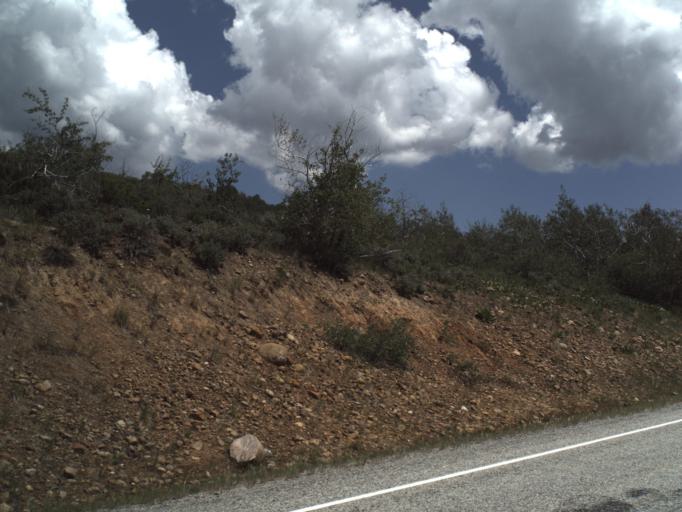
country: US
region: Utah
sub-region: Weber County
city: Wolf Creek
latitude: 41.4105
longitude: -111.5586
